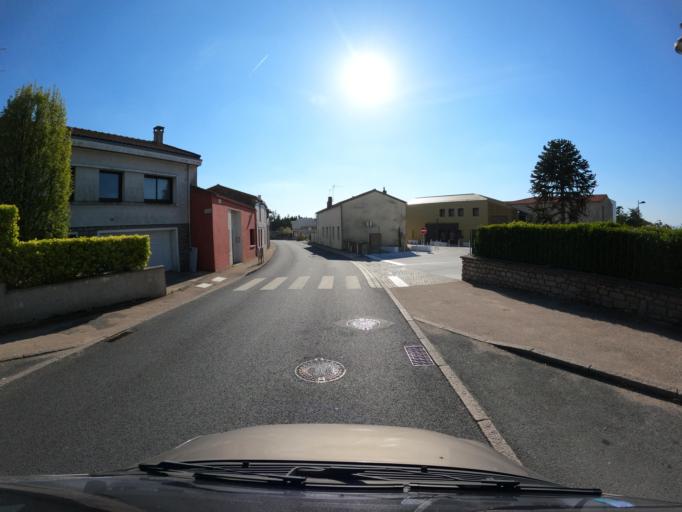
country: FR
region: Pays de la Loire
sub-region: Departement de la Vendee
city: La Gaubretiere
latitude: 46.9426
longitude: -1.0654
